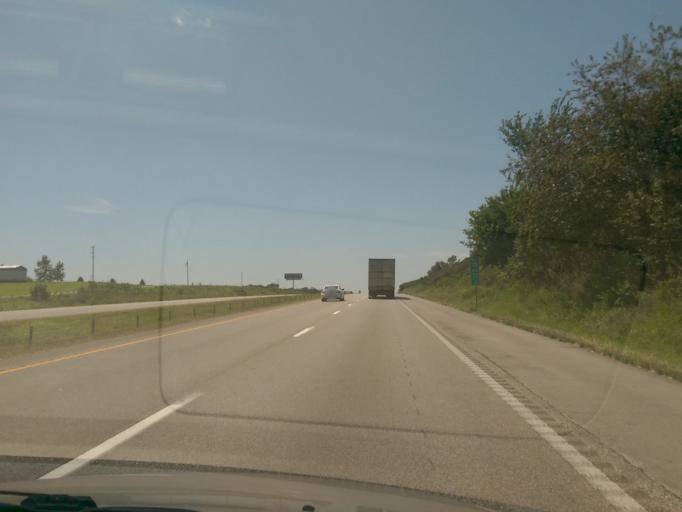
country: US
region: Missouri
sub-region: Saline County
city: Sweet Springs
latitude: 38.9729
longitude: -93.3101
